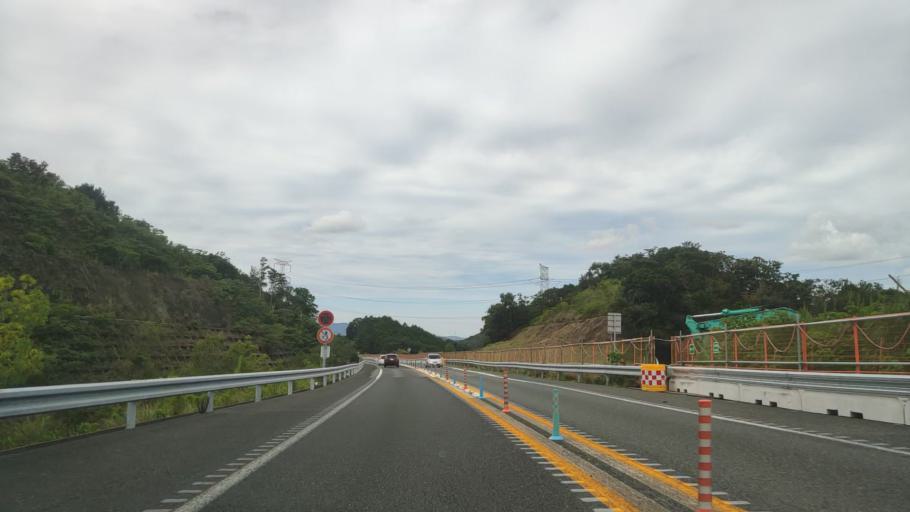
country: JP
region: Wakayama
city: Gobo
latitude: 33.8580
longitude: 135.2092
